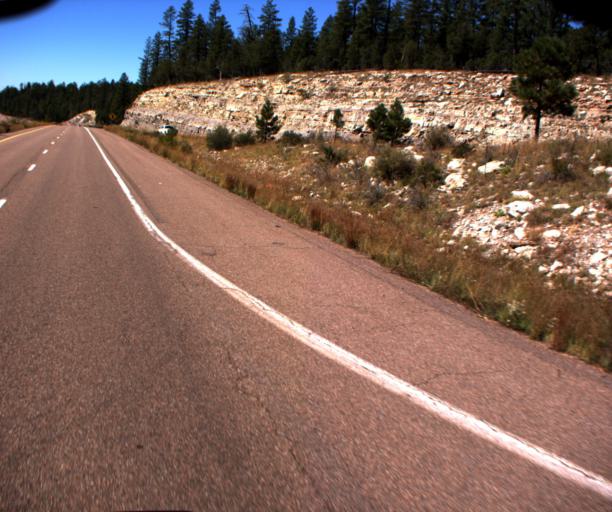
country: US
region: Arizona
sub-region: Gila County
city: Star Valley
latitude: 34.3143
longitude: -111.0331
